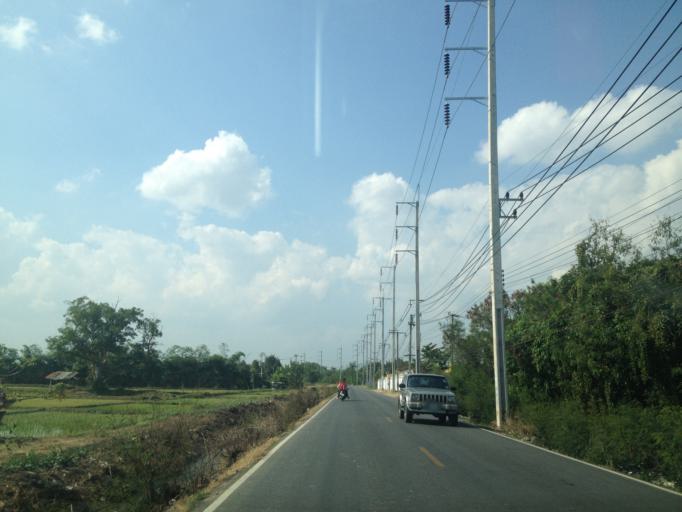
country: TH
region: Chiang Mai
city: Hang Dong
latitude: 18.6732
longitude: 98.9136
